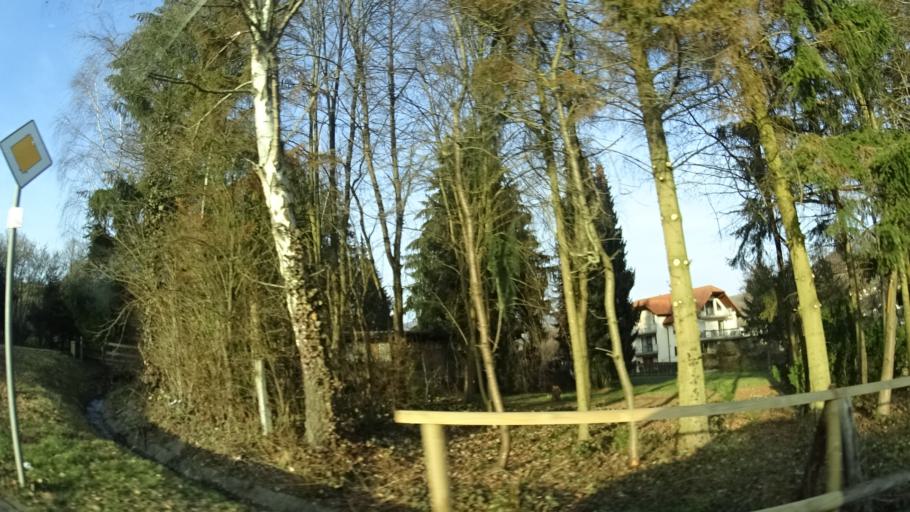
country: DE
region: Bavaria
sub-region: Regierungsbezirk Unterfranken
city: Zeitlofs
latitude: 50.3002
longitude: 9.6568
